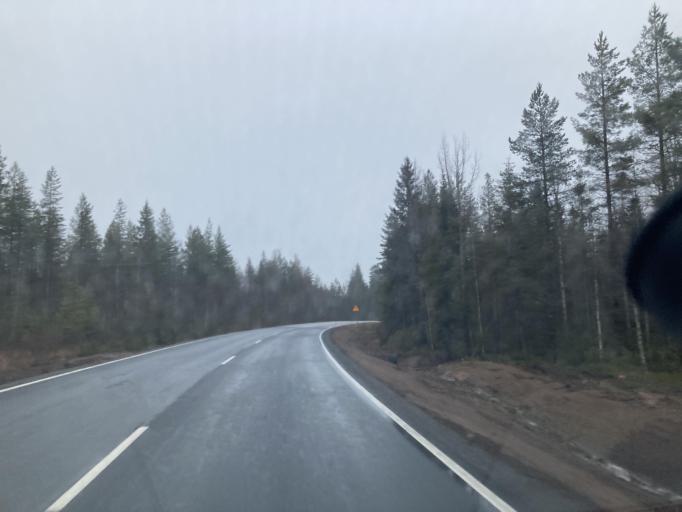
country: FI
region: Lapland
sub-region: Rovaniemi
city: Rovaniemi
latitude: 66.5922
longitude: 25.7932
